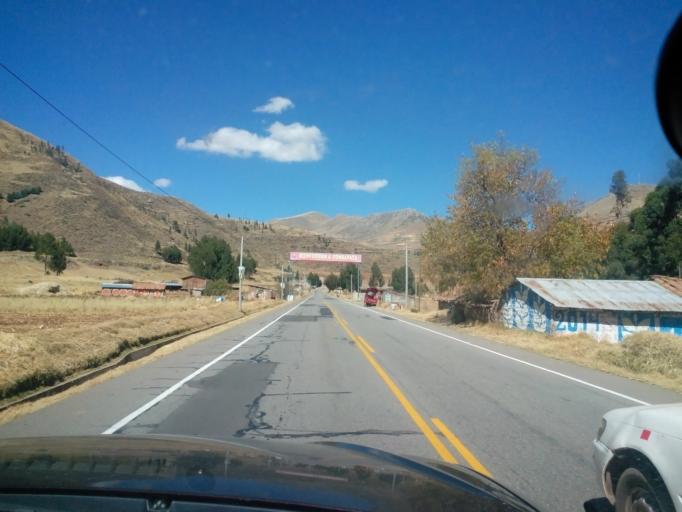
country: PE
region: Cusco
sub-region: Provincia de Canchis
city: Combapata
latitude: -14.0832
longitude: -71.4381
